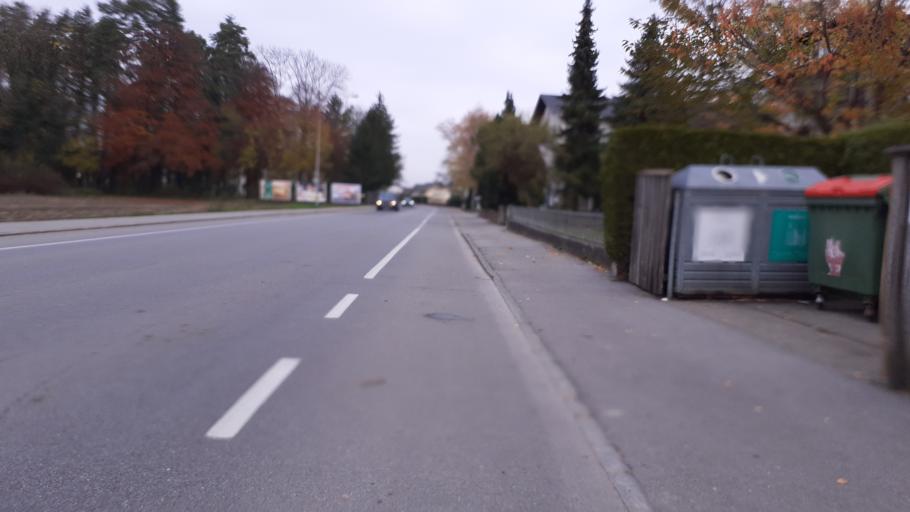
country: AT
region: Vorarlberg
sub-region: Politischer Bezirk Feldkirch
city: Nofels
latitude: 47.2513
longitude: 9.5877
